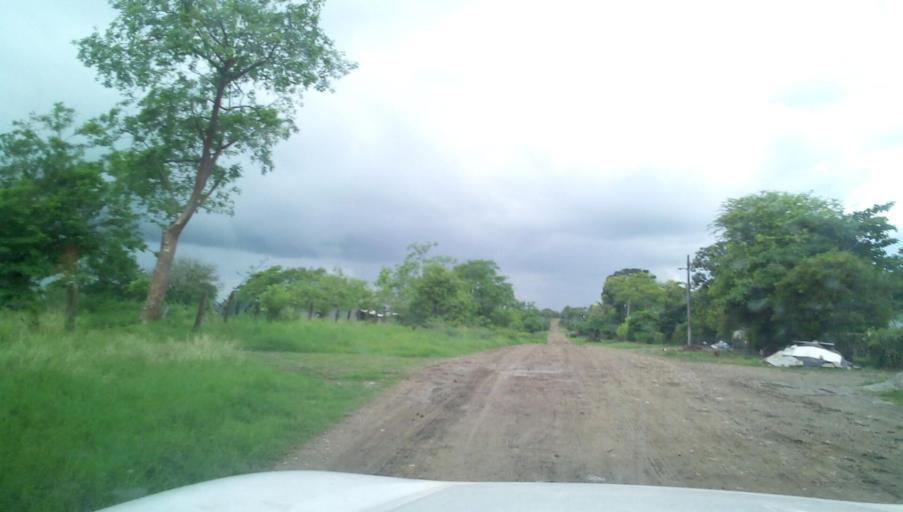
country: MX
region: Veracruz
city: Panuco
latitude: 21.7998
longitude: -98.1008
